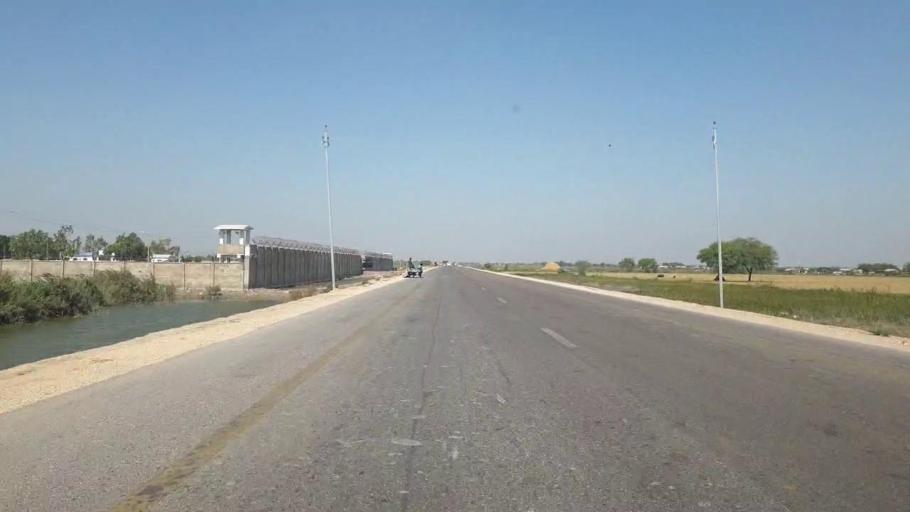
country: PK
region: Sindh
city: Talhar
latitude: 24.8346
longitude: 68.8161
